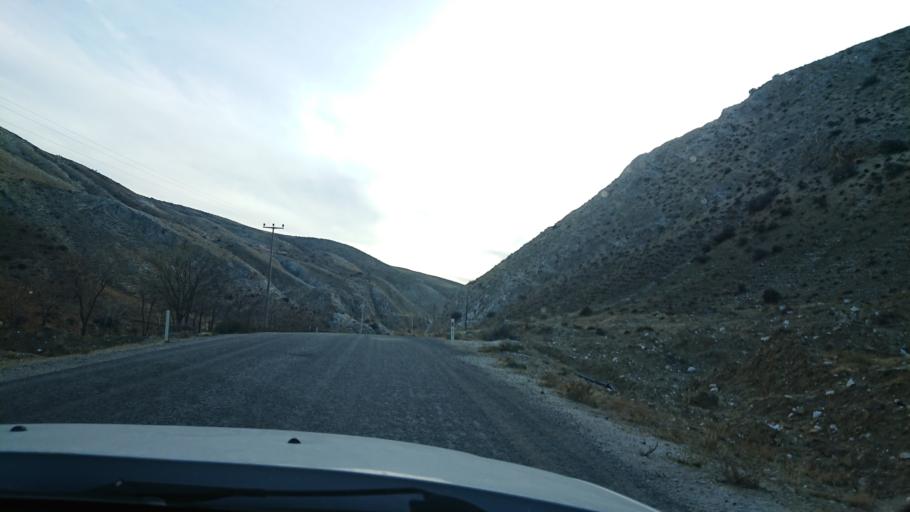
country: TR
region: Ankara
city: Sereflikochisar
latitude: 38.7539
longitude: 33.6925
